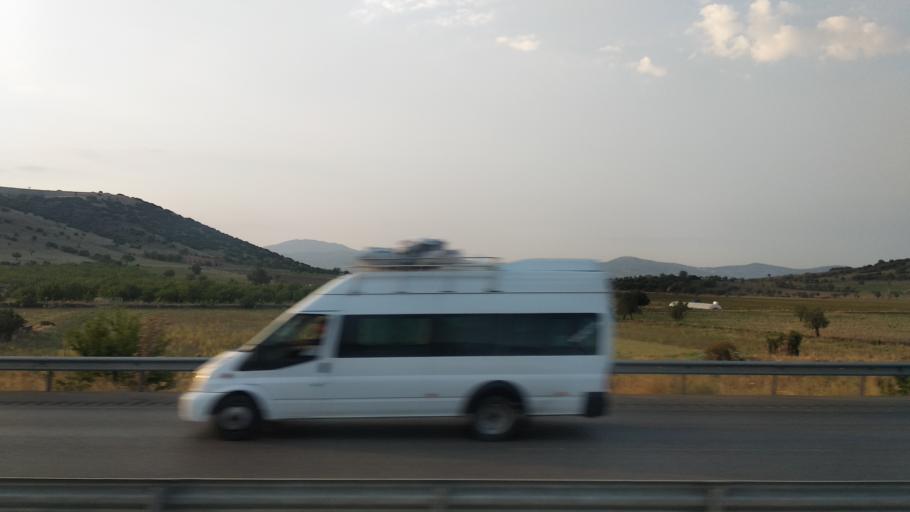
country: TR
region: Manisa
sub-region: Kula
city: Kula
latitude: 38.5565
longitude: 28.6963
